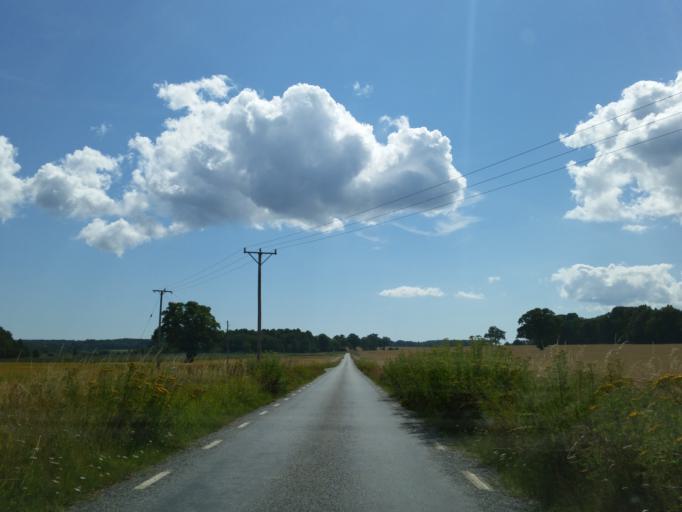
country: SE
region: Stockholm
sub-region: Sodertalje Kommun
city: Pershagen
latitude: 59.0501
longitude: 17.6595
